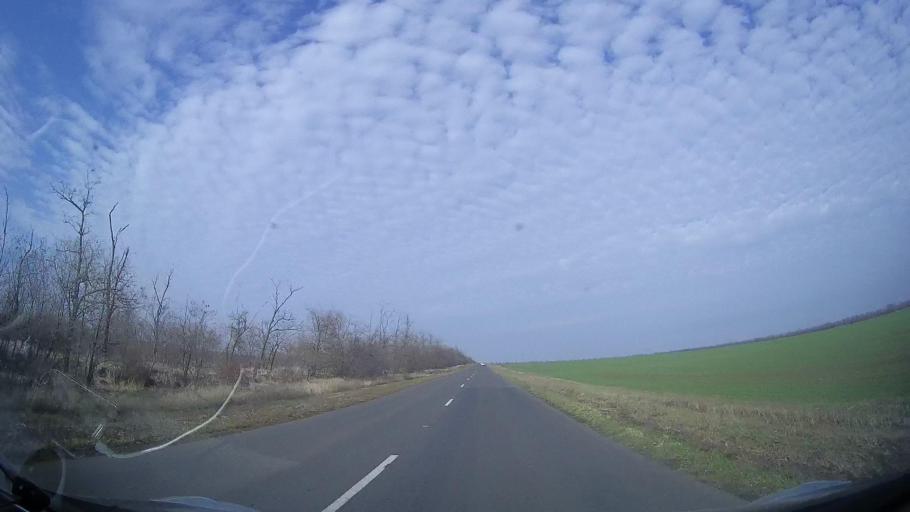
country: RU
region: Rostov
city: Gigant
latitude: 46.8488
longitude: 41.2857
